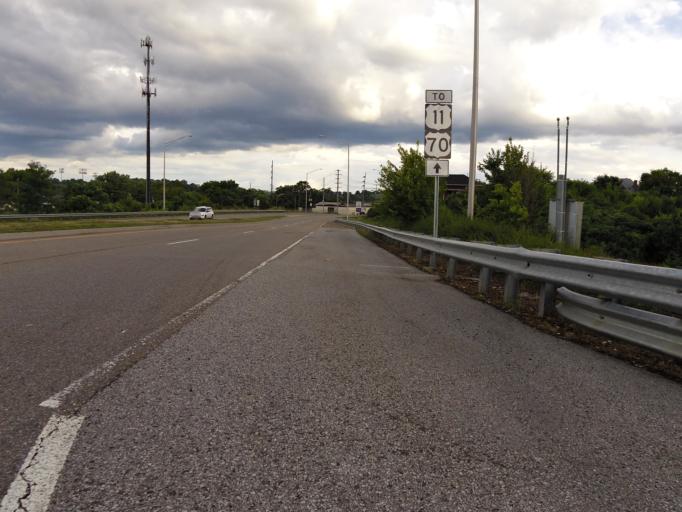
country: US
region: Tennessee
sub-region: Knox County
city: Knoxville
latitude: 35.9823
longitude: -83.9171
